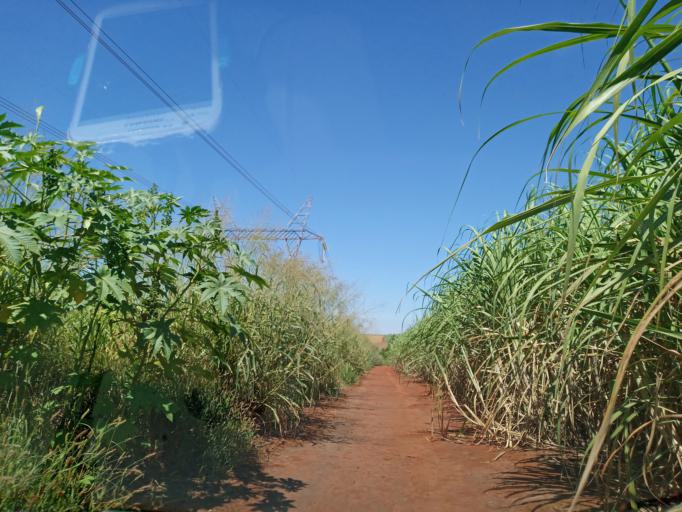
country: BR
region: Goias
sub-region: Itumbiara
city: Itumbiara
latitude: -18.4435
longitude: -49.1389
